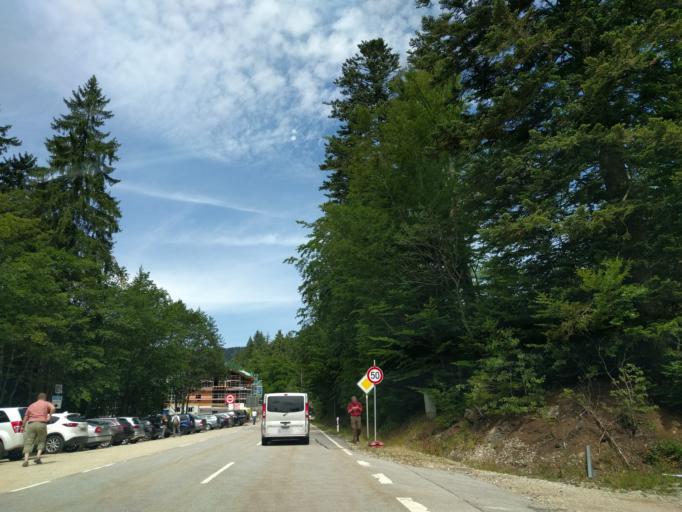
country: DE
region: Bavaria
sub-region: Lower Bavaria
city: Bayerisch Eisenstein
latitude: 49.0981
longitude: 13.1608
